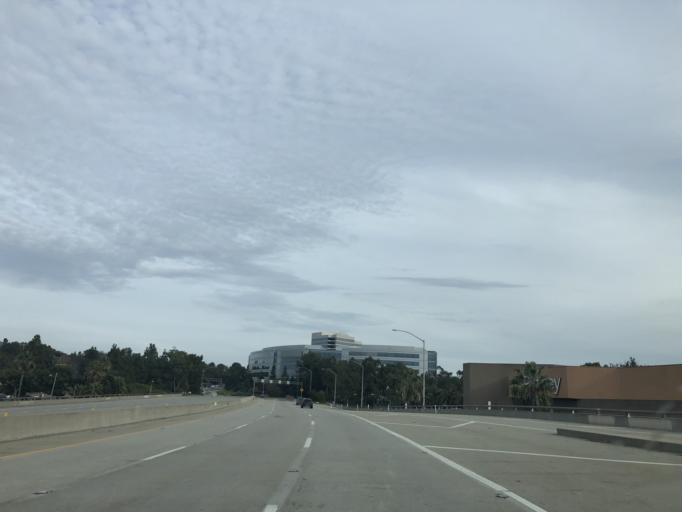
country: US
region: California
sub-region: Los Angeles County
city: Ladera Heights
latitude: 33.9872
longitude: -118.3929
